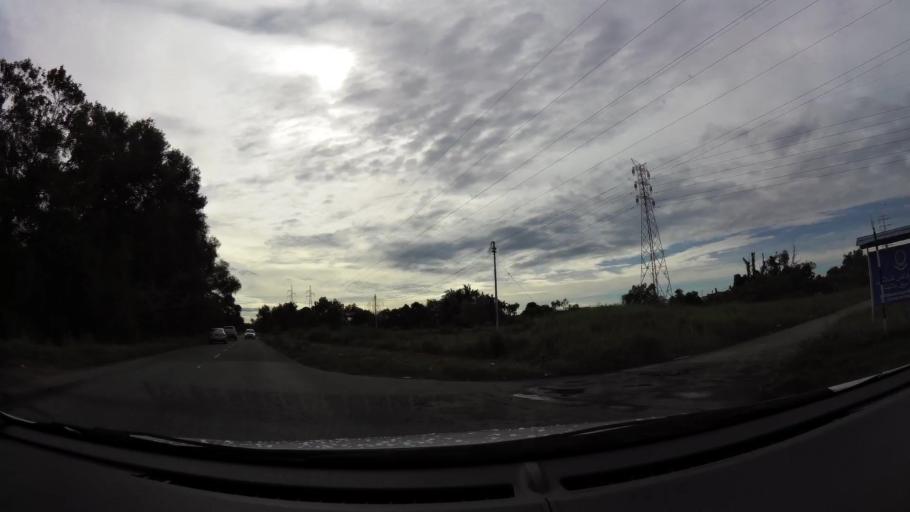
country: BN
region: Belait
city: Seria
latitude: 4.6171
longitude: 114.3458
